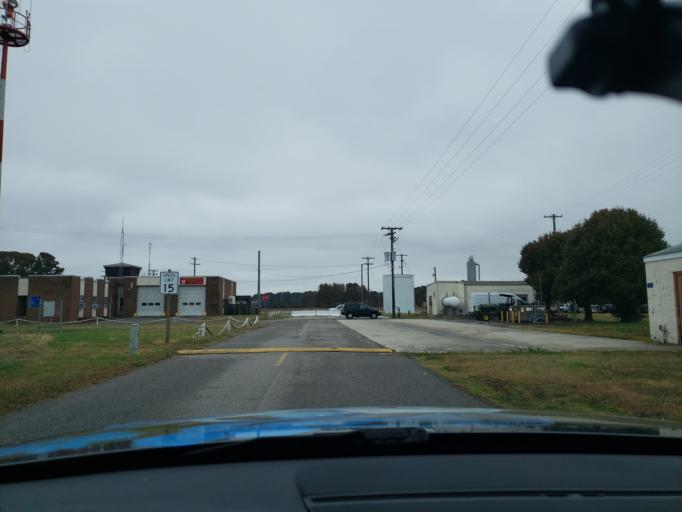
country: US
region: Virginia
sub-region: City of Chesapeake
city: Chesapeake
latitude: 36.7065
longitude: -76.1285
